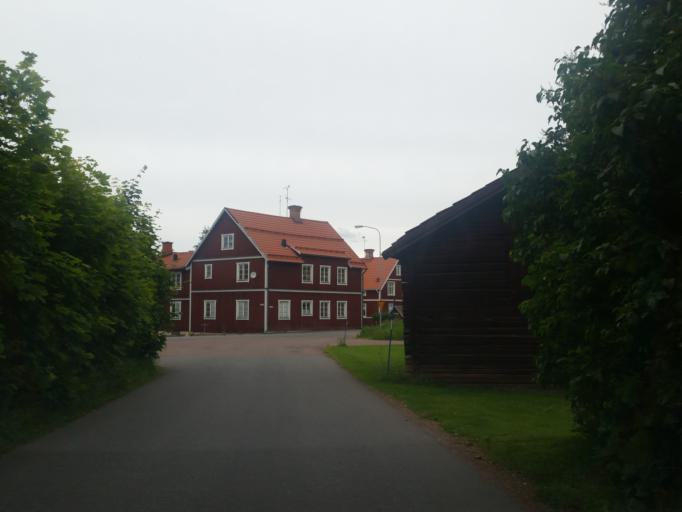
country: SE
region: Dalarna
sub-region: Leksand Municipality
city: Smedby
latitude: 60.6765
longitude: 15.0950
